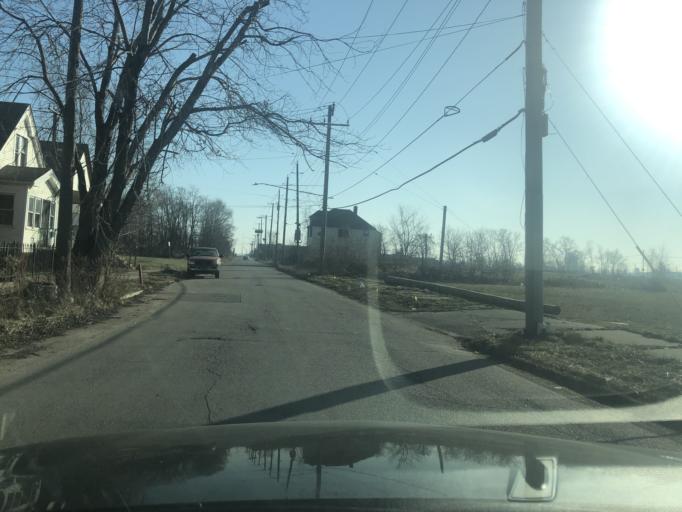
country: US
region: Michigan
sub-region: Wayne County
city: River Rouge
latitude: 42.3079
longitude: -83.0996
